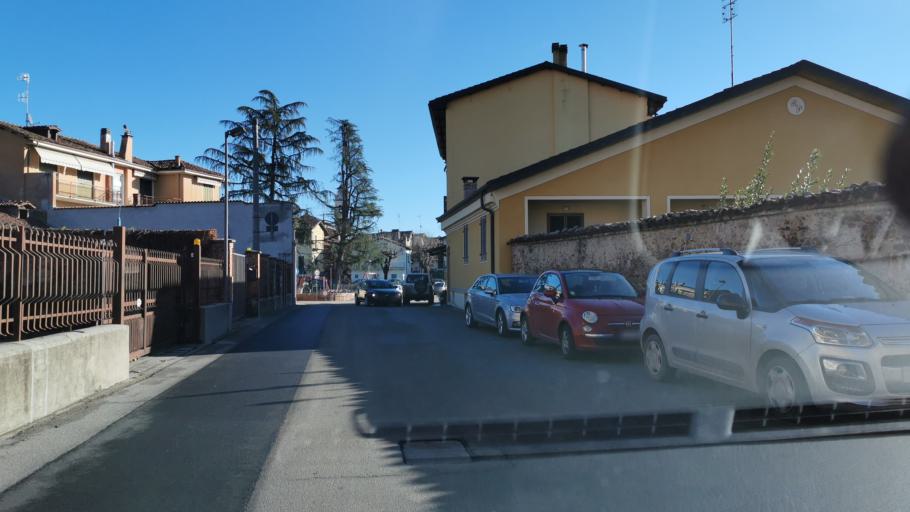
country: IT
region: Piedmont
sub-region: Provincia di Cuneo
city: Carru
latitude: 44.4783
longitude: 7.8759
